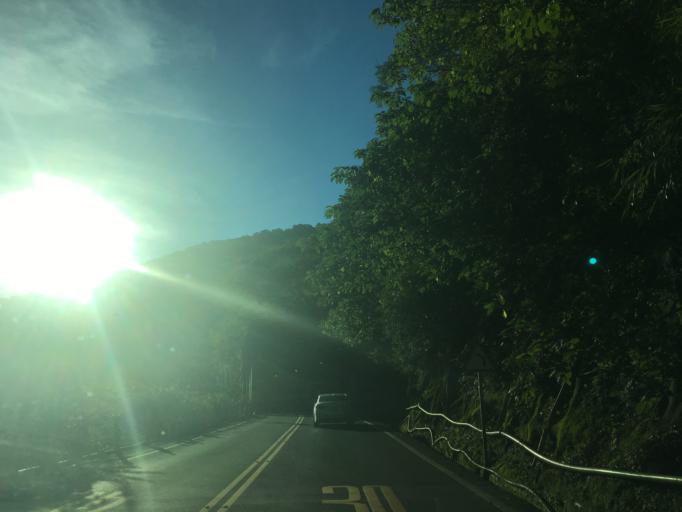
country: TW
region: Taiwan
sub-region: Nantou
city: Puli
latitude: 23.9978
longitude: 121.0477
